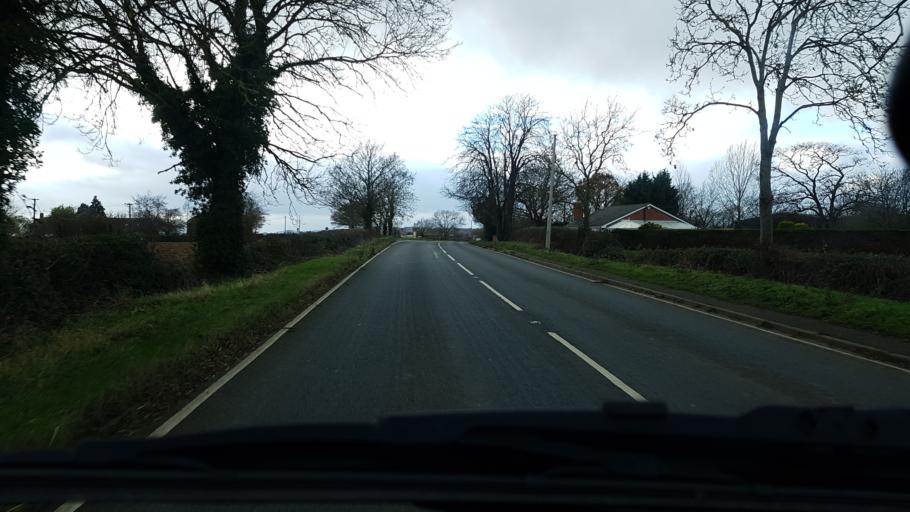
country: GB
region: England
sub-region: Worcestershire
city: Bredon
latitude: 52.0820
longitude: -2.1298
